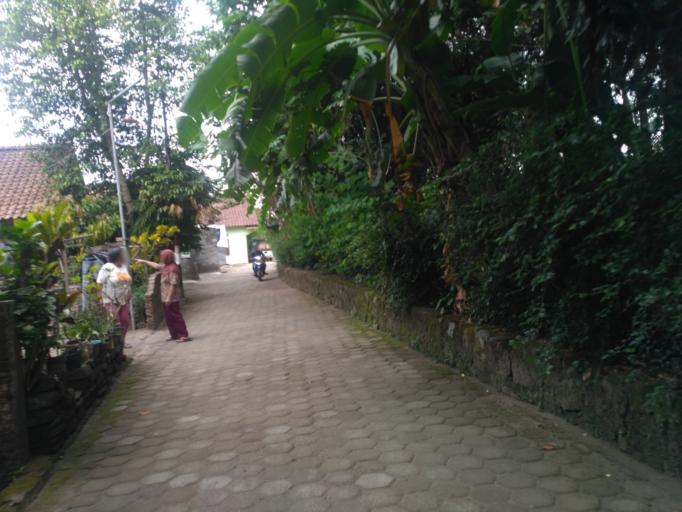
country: ID
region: Daerah Istimewa Yogyakarta
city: Melati
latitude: -7.7536
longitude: 110.3659
